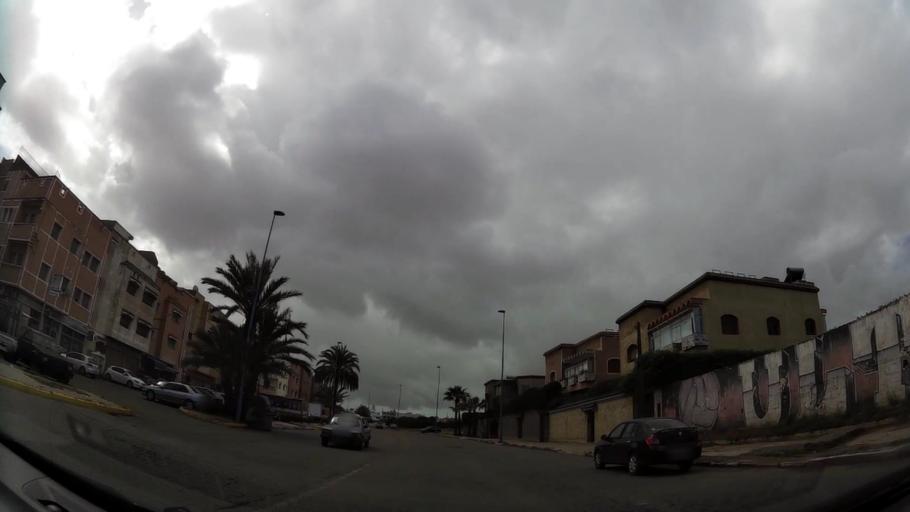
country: MA
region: Grand Casablanca
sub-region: Casablanca
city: Casablanca
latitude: 33.5443
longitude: -7.6023
